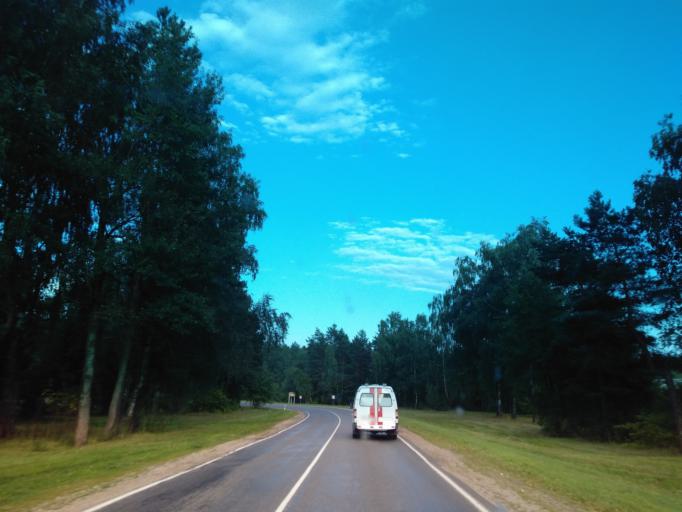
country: BY
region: Minsk
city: Uzda
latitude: 53.4183
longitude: 27.4125
